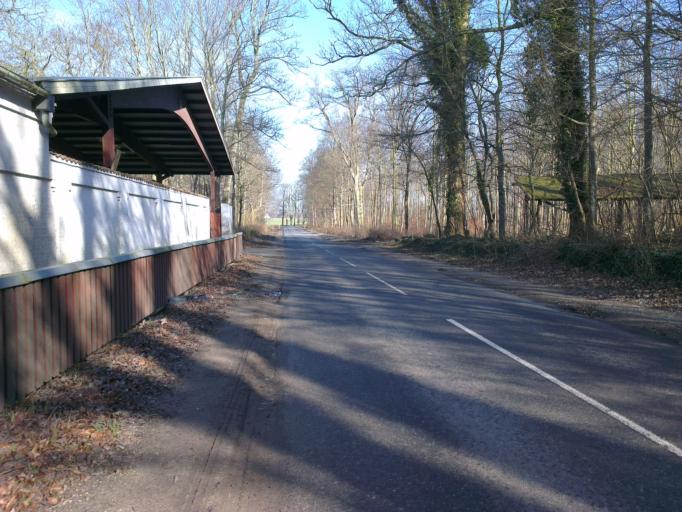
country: DK
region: Capital Region
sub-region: Frederikssund Kommune
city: Skibby
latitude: 55.7836
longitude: 11.9428
